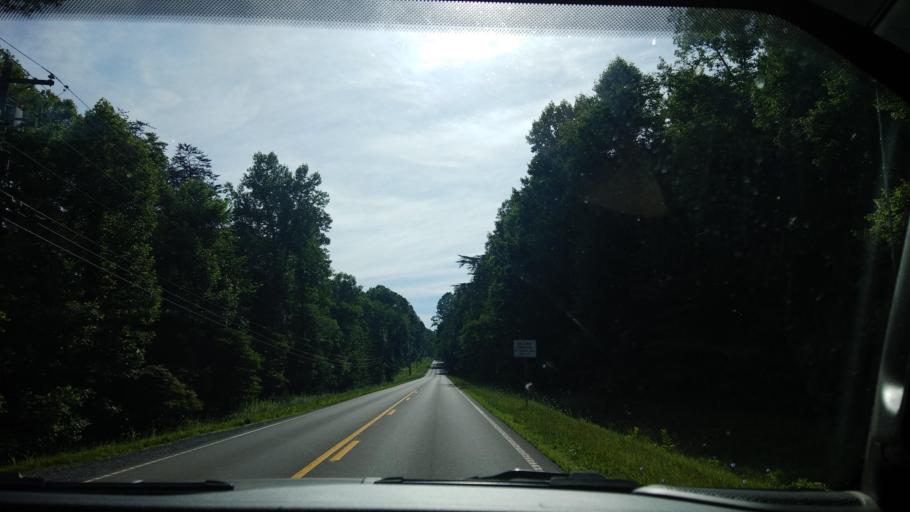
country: US
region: Tennessee
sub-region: Sevier County
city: Gatlinburg
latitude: 35.7603
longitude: -83.3398
